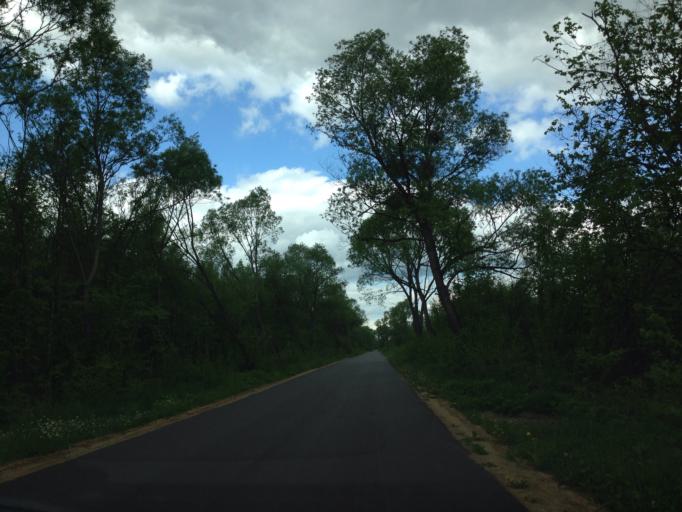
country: PL
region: Podlasie
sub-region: Powiat bialostocki
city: Tykocin
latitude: 53.3102
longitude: 22.6032
